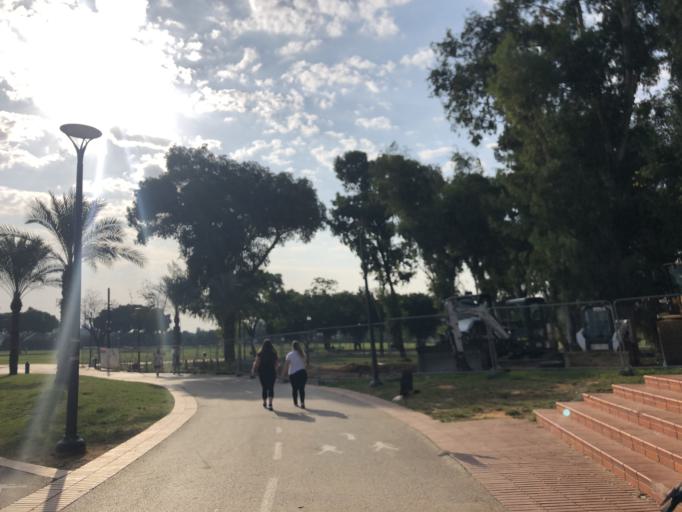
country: IL
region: Tel Aviv
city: Giv`atayim
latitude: 32.0493
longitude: 34.8233
